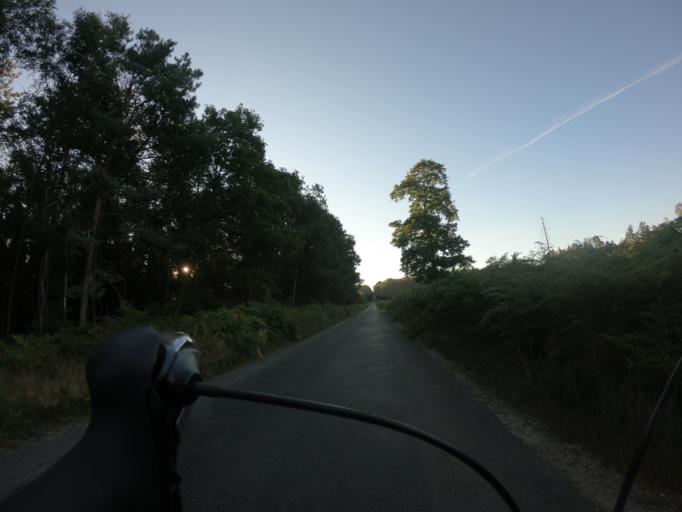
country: FR
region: Lower Normandy
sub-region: Departement de l'Orne
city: Magny-le-Desert
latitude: 48.5445
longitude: -0.3523
